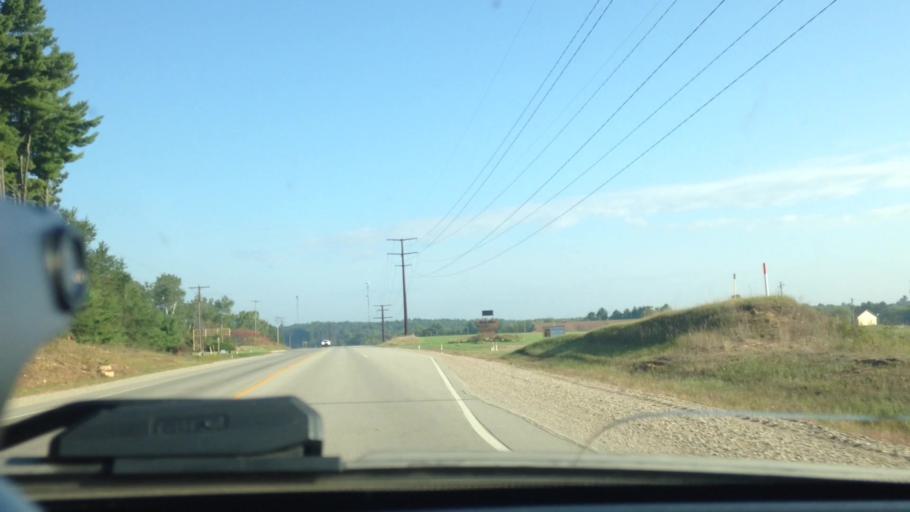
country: US
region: Wisconsin
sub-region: Marinette County
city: Peshtigo
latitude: 45.2016
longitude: -87.9943
